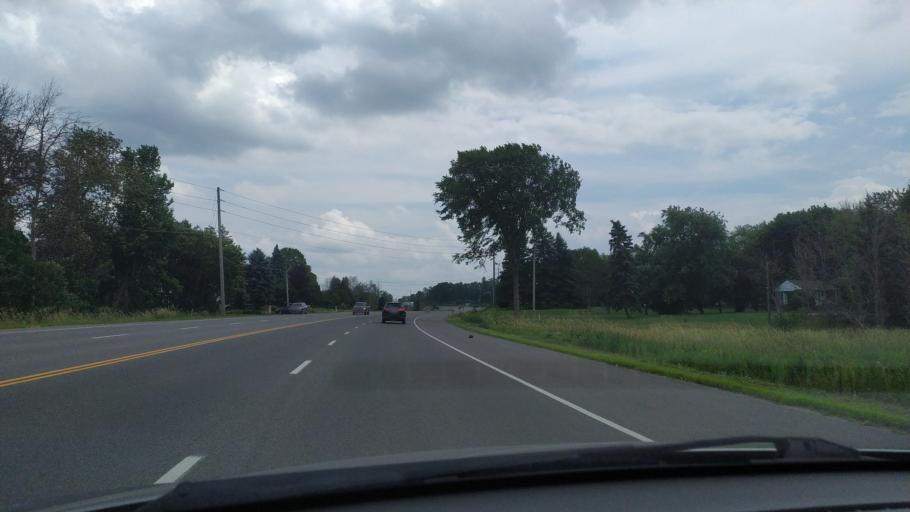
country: CA
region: Ontario
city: Stratford
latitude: 43.3705
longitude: -80.9248
